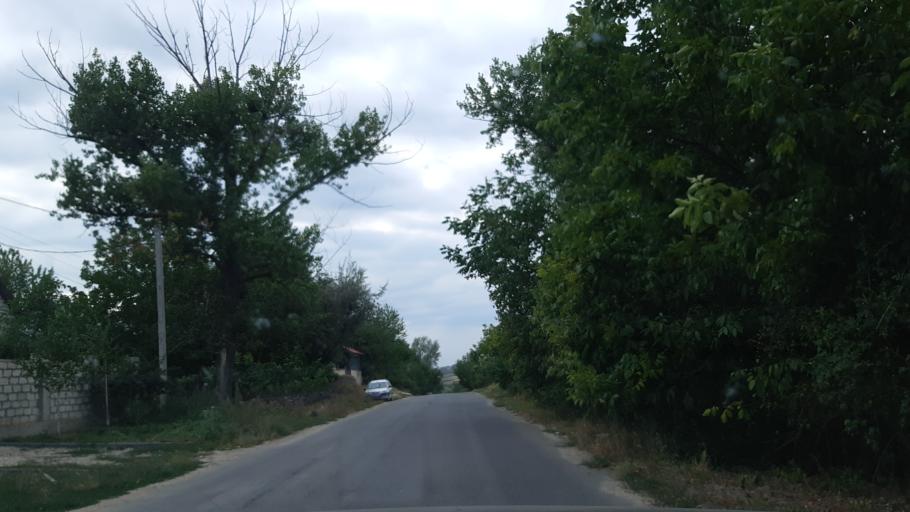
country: MD
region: Chisinau
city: Vatra
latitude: 47.0538
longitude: 28.7315
